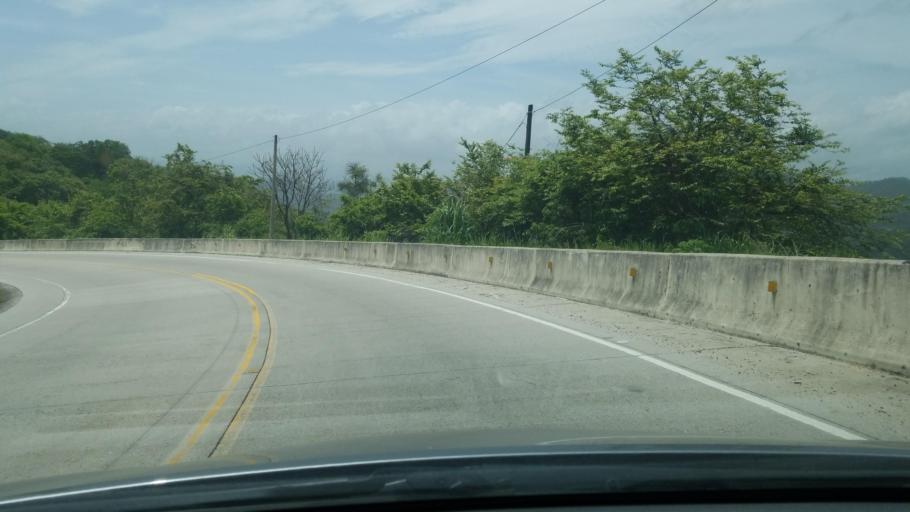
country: HN
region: Copan
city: Veracruz
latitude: 14.9115
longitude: -88.7542
